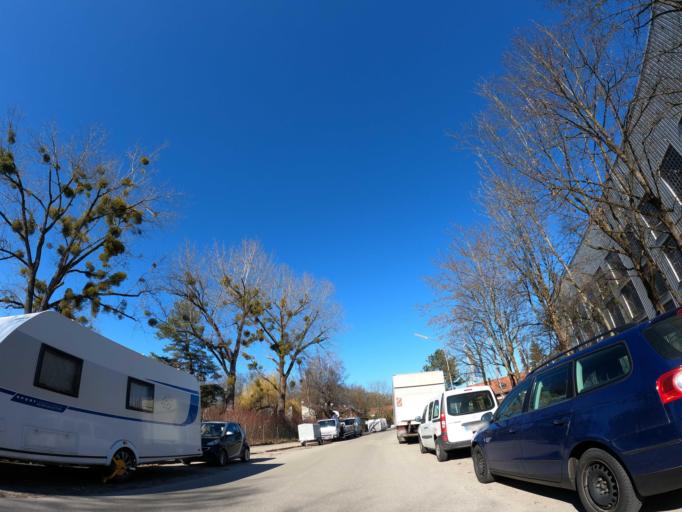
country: DE
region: Bavaria
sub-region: Upper Bavaria
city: Unterhaching
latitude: 48.0896
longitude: 11.6279
